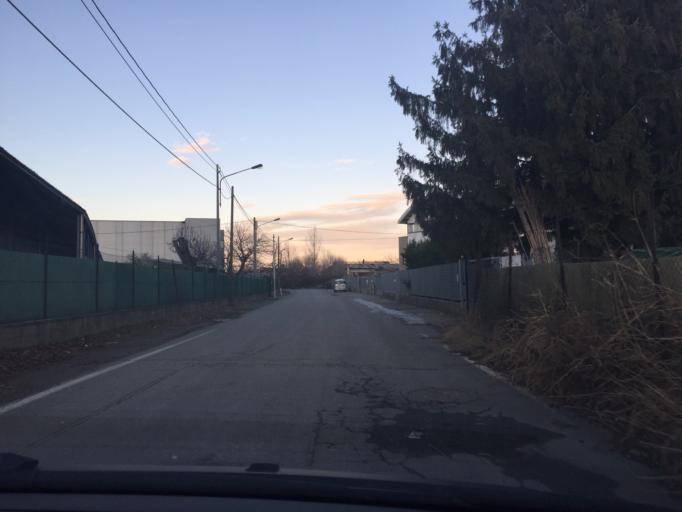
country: IT
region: Piedmont
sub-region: Provincia di Torino
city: Grugliasco
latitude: 45.0585
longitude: 7.5898
